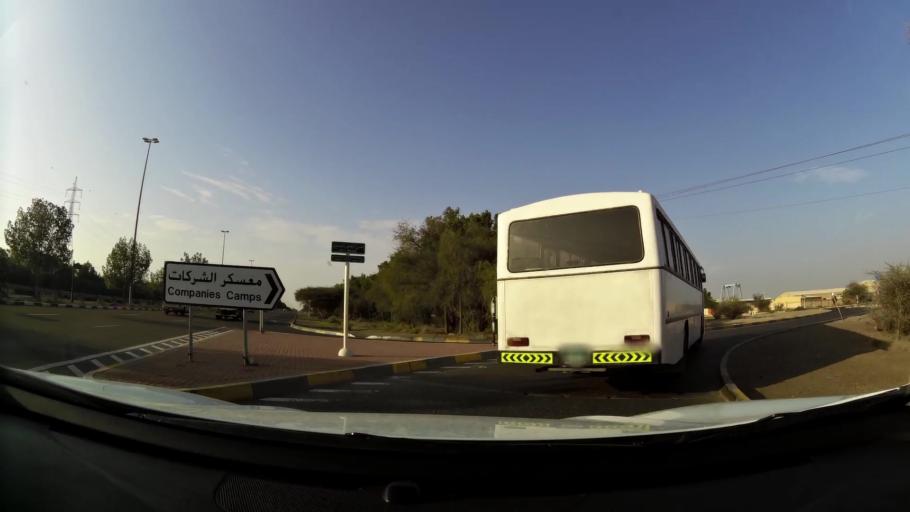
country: AE
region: Abu Dhabi
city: Al Ain
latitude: 24.1395
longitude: 55.8155
